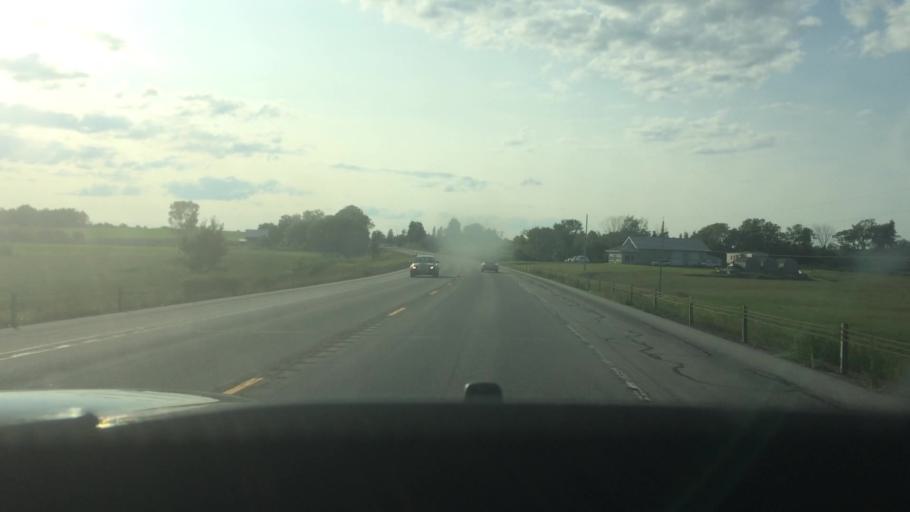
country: US
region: New York
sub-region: St. Lawrence County
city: Canton
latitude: 44.6309
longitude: -75.2438
